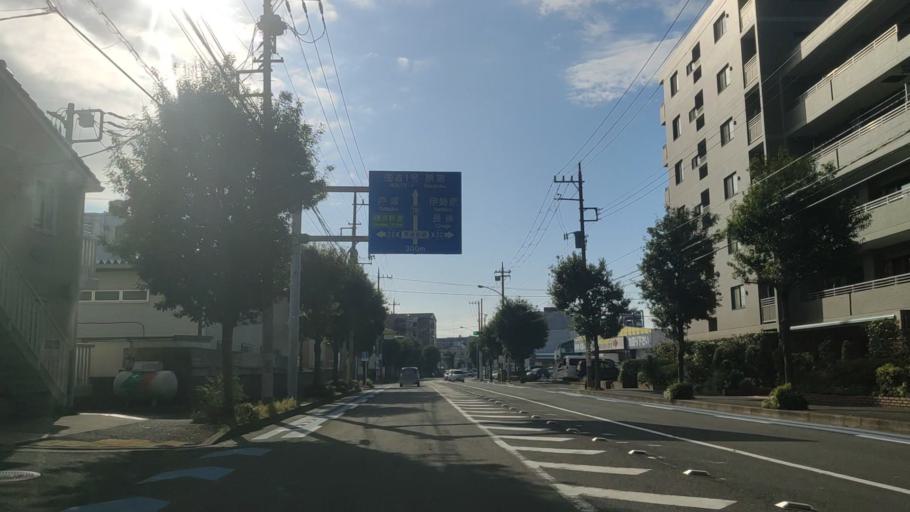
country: JP
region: Kanagawa
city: Minami-rinkan
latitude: 35.4199
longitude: 139.4853
